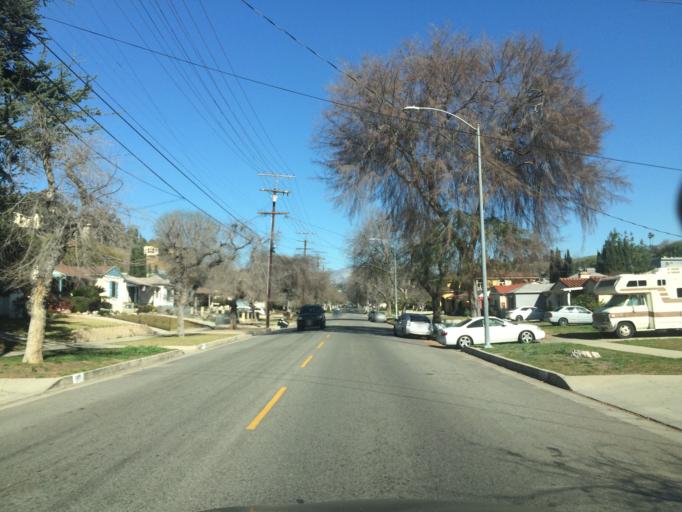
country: US
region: California
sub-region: Los Angeles County
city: South Pasadena
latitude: 34.0895
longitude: -118.1832
